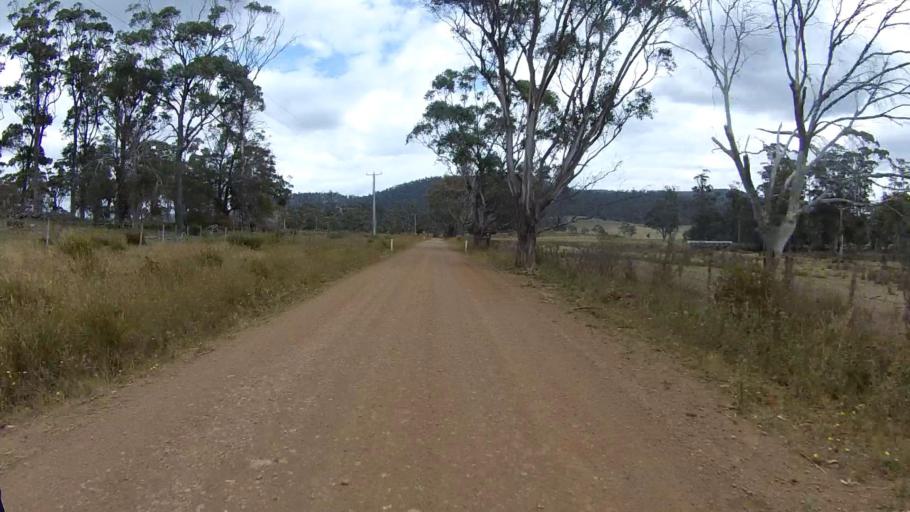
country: AU
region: Tasmania
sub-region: Sorell
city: Sorell
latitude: -42.6429
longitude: 147.9031
